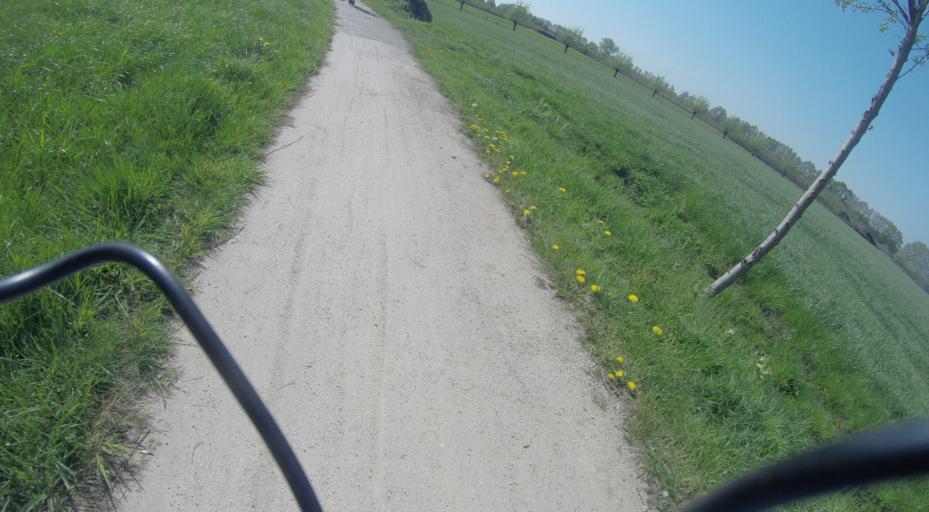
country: NL
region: Gelderland
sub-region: Oost Gelre
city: Lichtenvoorde
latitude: 52.0029
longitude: 6.5296
